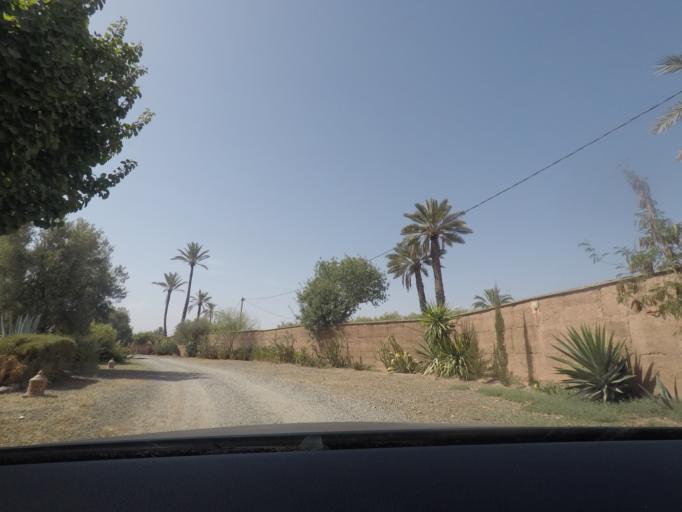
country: MA
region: Marrakech-Tensift-Al Haouz
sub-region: Marrakech
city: Marrakesh
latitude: 31.5800
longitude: -8.0280
